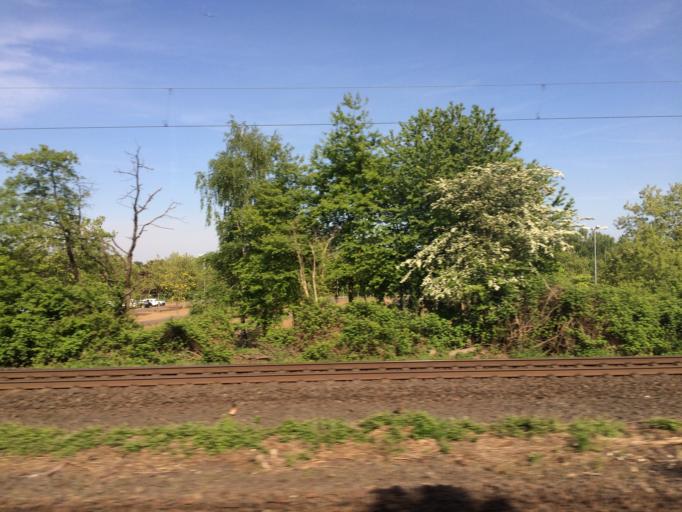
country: DE
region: North Rhine-Westphalia
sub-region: Regierungsbezirk Koln
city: Leverkusen
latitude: 51.0192
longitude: 6.9947
